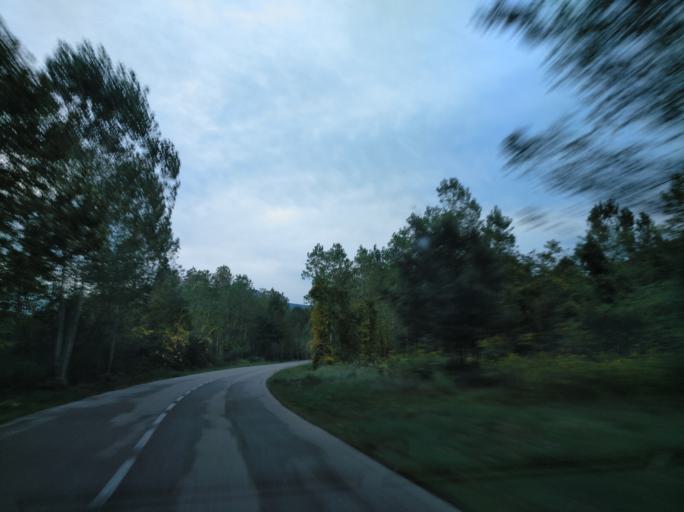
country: ES
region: Catalonia
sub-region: Provincia de Girona
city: Angles
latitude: 41.9634
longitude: 2.6541
